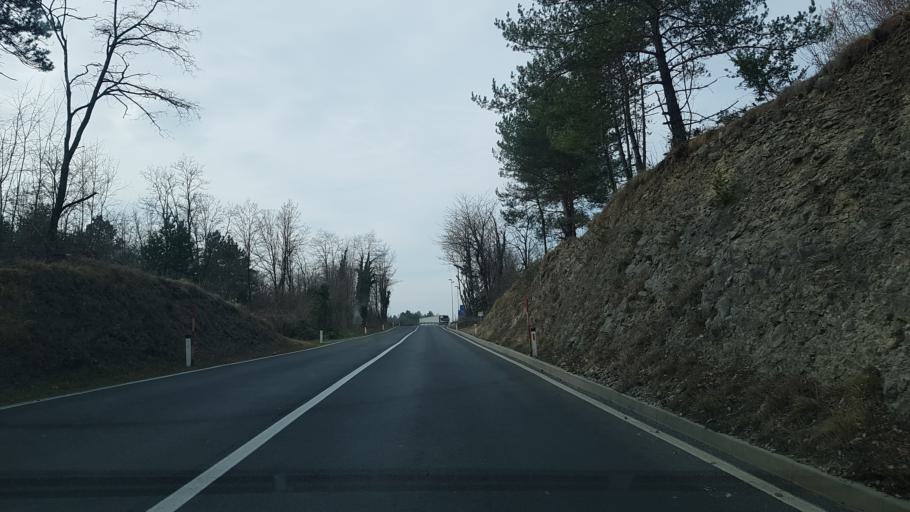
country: SI
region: Ilirska Bistrica
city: Ilirska Bistrica
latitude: 45.4913
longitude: 14.2053
